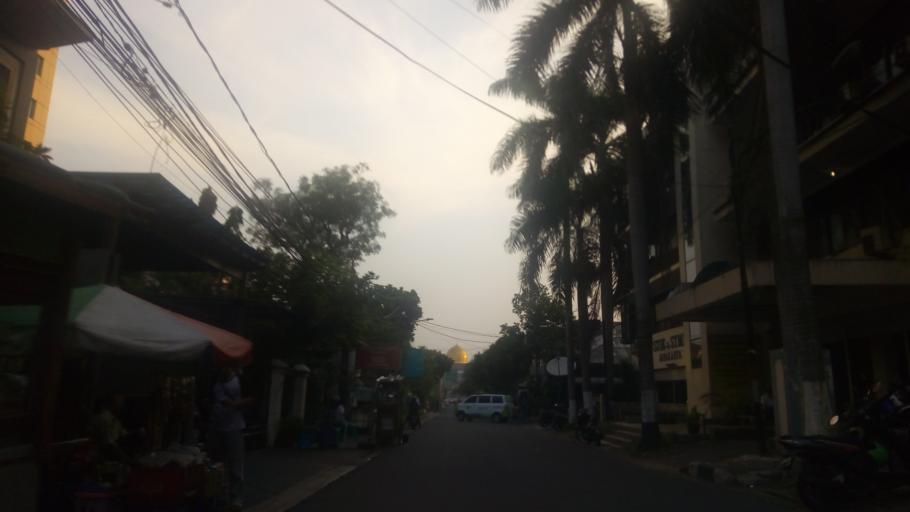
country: ID
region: Jakarta Raya
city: Jakarta
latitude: -6.1985
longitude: 106.8511
